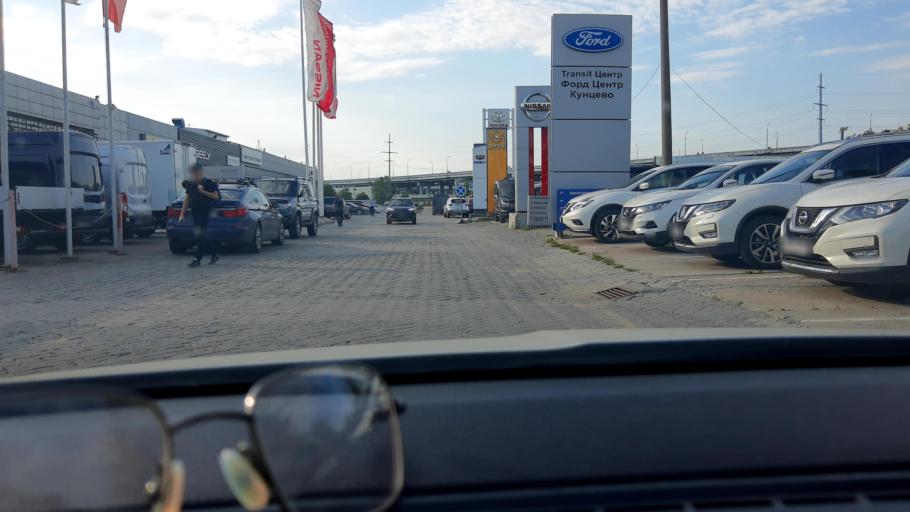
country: RU
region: Moskovskaya
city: Nemchinovka
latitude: 55.7262
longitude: 37.3755
